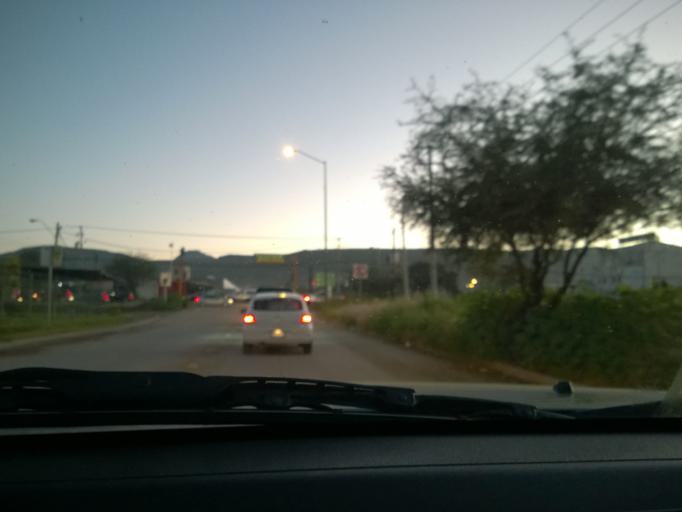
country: MX
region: Guanajuato
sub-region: Leon
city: Fraccionamiento Paraiso Real
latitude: 21.1082
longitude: -101.5924
